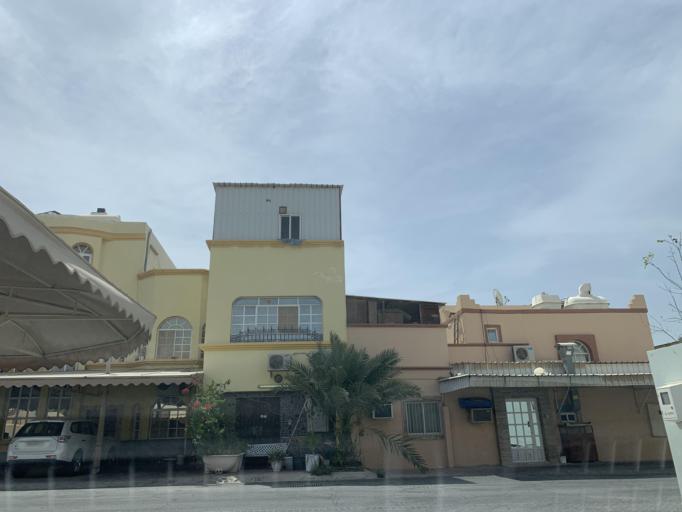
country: BH
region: Northern
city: Ar Rifa'
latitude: 26.1437
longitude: 50.5650
